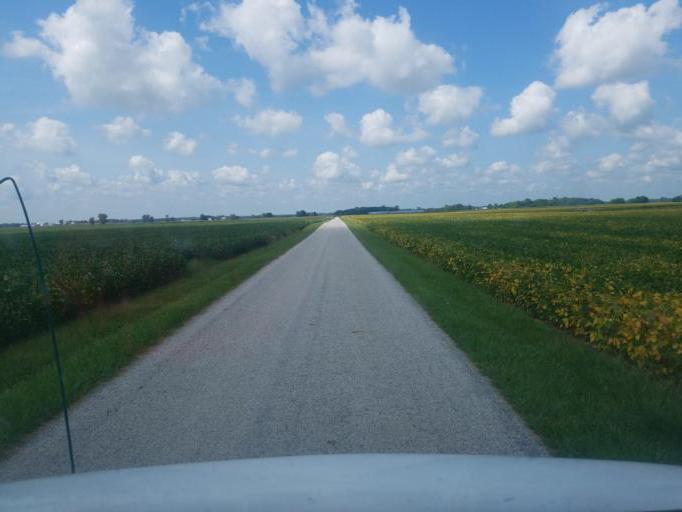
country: US
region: Ohio
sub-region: Marion County
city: Prospect
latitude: 40.4221
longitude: -83.1435
